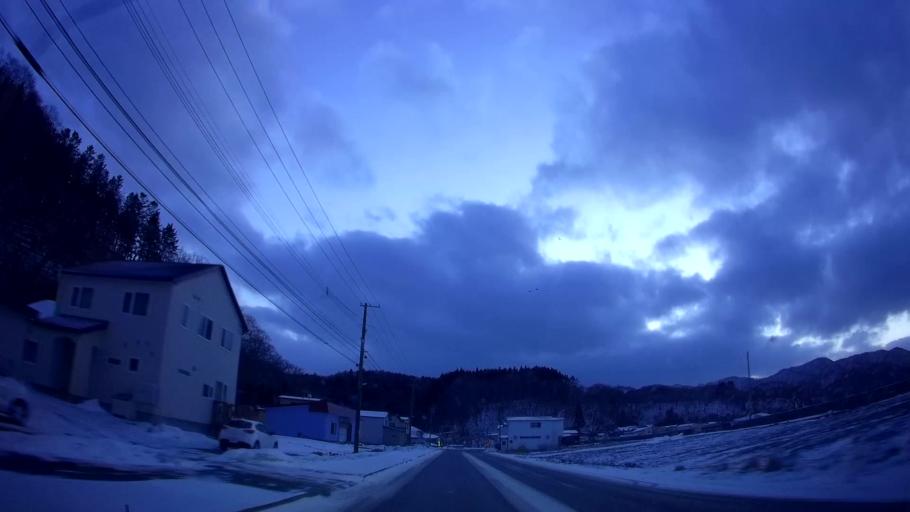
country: JP
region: Hokkaido
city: Hakodate
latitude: 41.8940
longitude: 141.0307
